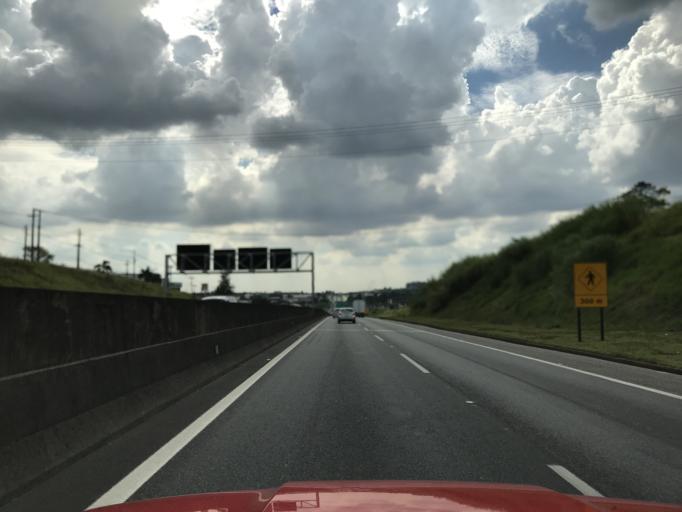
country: BR
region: Sao Paulo
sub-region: Valinhos
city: Valinhos
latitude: -22.9998
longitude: -47.0315
